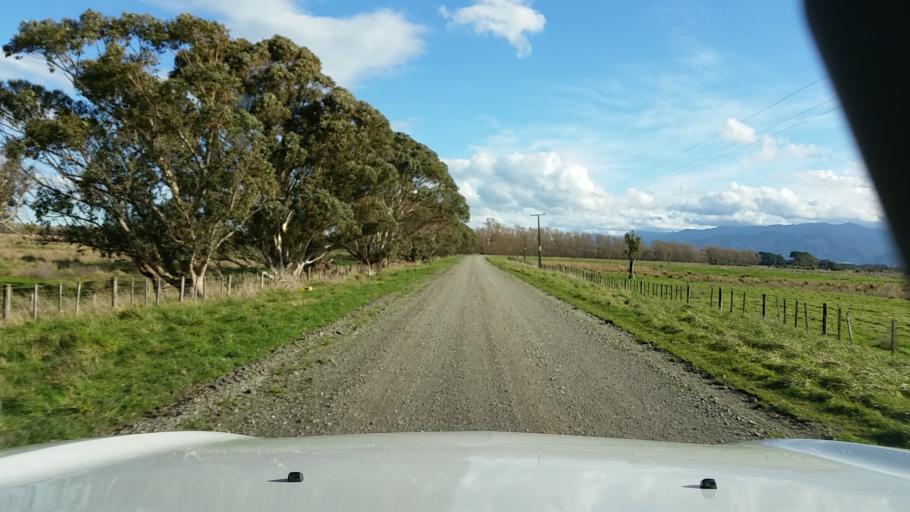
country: NZ
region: Wellington
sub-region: Upper Hutt City
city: Upper Hutt
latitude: -41.2470
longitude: 175.2588
